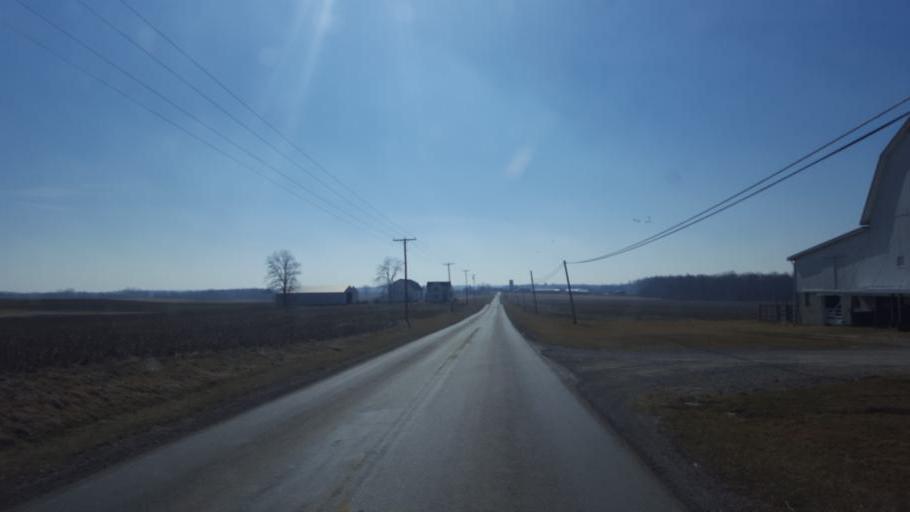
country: US
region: Ohio
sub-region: Richland County
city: Shelby
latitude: 40.9369
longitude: -82.5820
